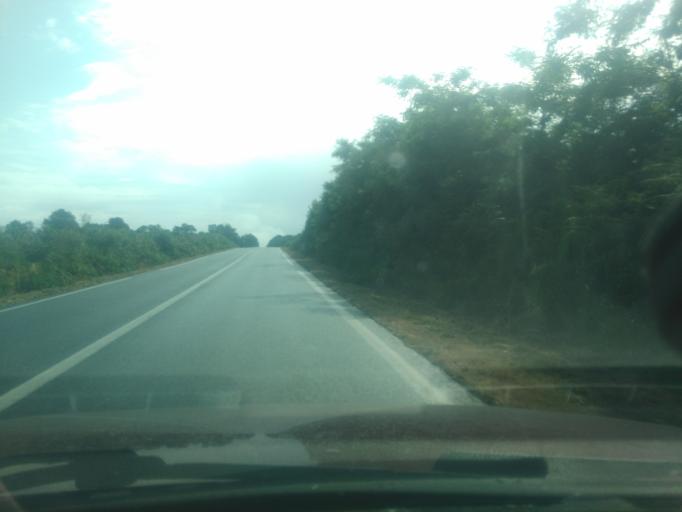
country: FR
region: Poitou-Charentes
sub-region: Departement des Deux-Sevres
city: Secondigny
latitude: 46.6132
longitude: -0.3960
